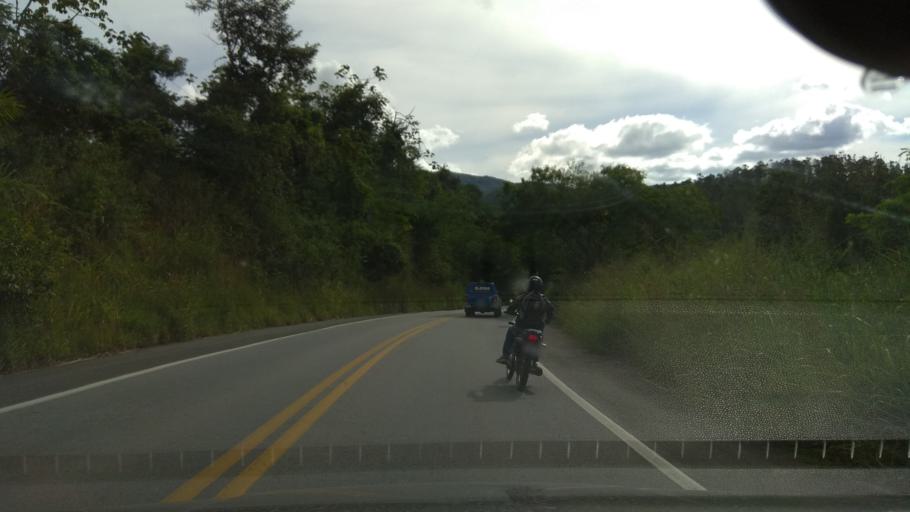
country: BR
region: Bahia
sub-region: Jitauna
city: Jitauna
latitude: -14.0085
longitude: -39.9142
